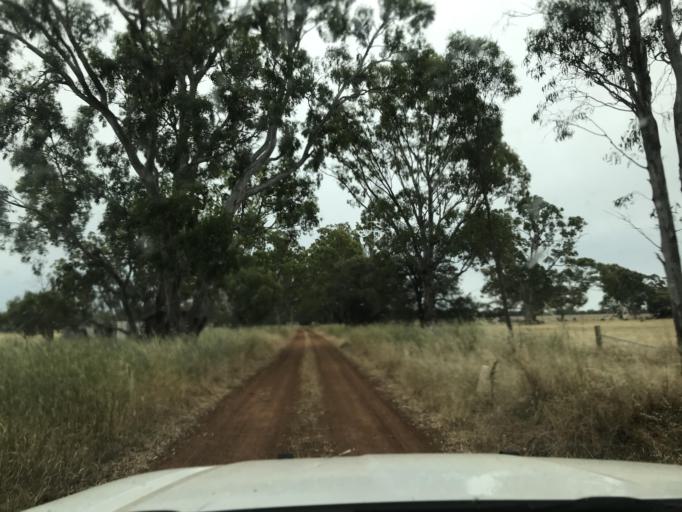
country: AU
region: Victoria
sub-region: Horsham
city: Horsham
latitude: -37.0658
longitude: 141.6831
